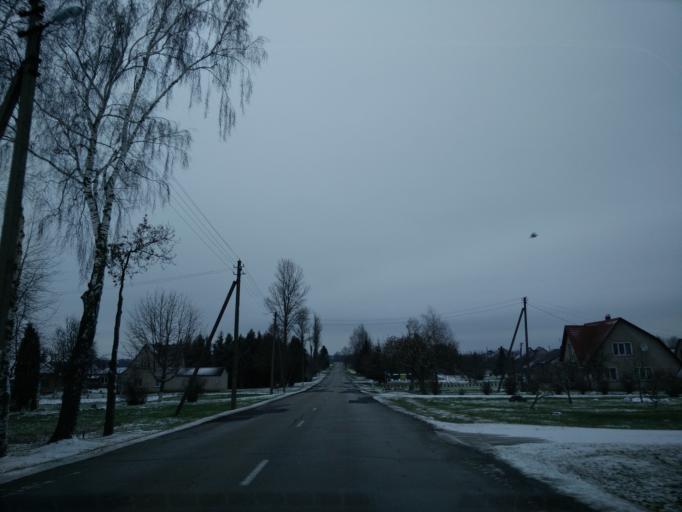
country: LT
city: Ariogala
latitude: 55.4244
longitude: 23.3473
